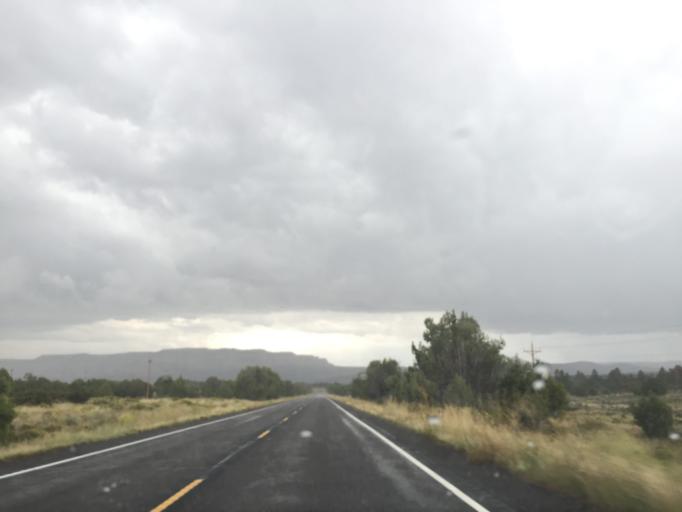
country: US
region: Utah
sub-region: Kane County
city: Kanab
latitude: 37.2256
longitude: -112.7229
